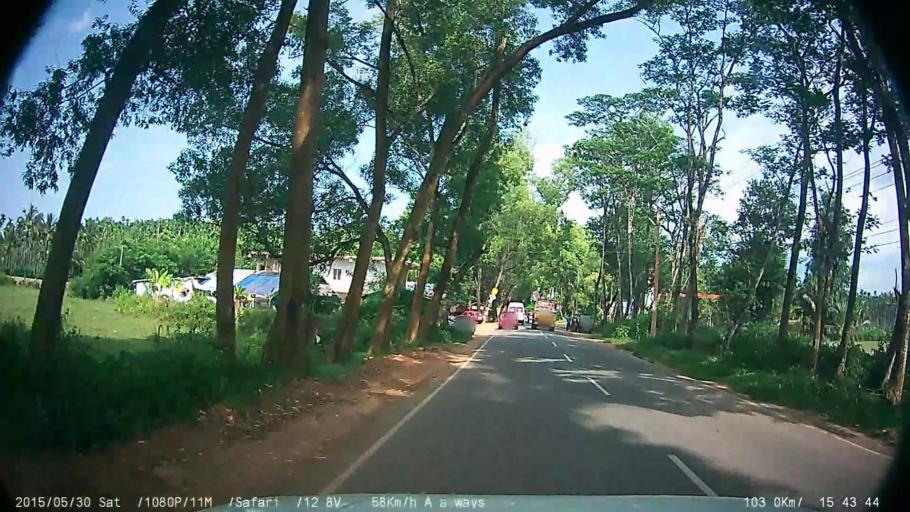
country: IN
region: Kerala
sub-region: Wayanad
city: Panamaram
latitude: 11.7278
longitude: 76.0759
